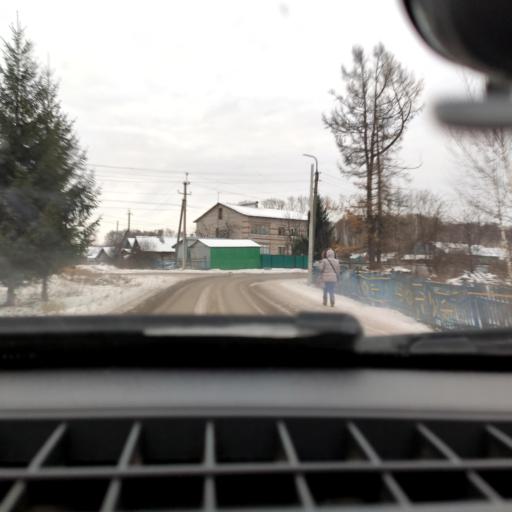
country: RU
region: Bashkortostan
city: Iglino
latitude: 54.8348
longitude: 56.4248
